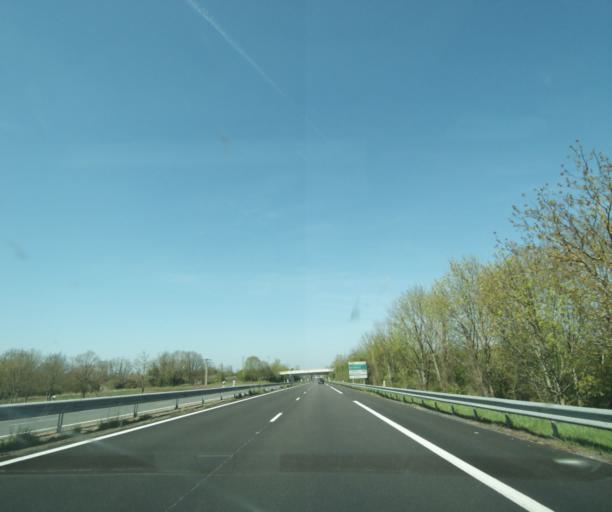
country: FR
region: Bourgogne
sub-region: Departement de la Nievre
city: La Charite-sur-Loire
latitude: 47.1956
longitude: 3.0248
